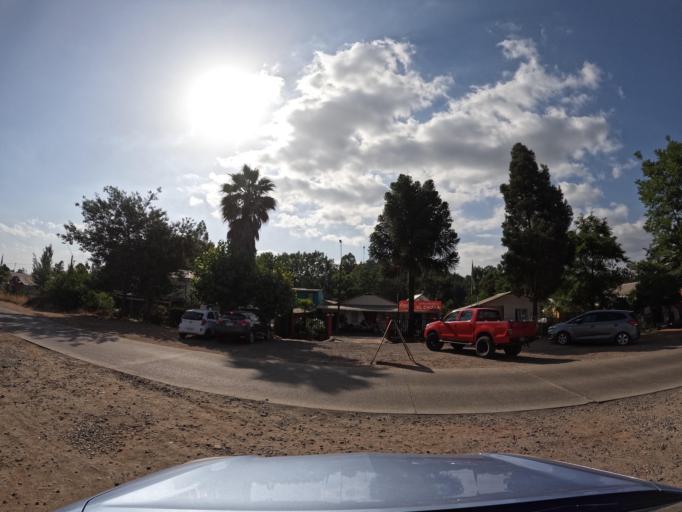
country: CL
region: Maule
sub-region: Provincia de Curico
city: Molina
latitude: -35.2795
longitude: -71.2580
